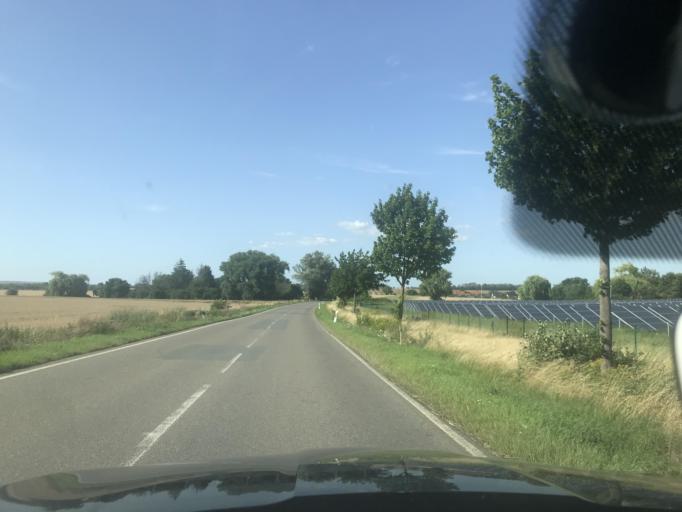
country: DE
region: Saxony-Anhalt
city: Wegeleben
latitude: 51.8825
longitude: 11.1610
